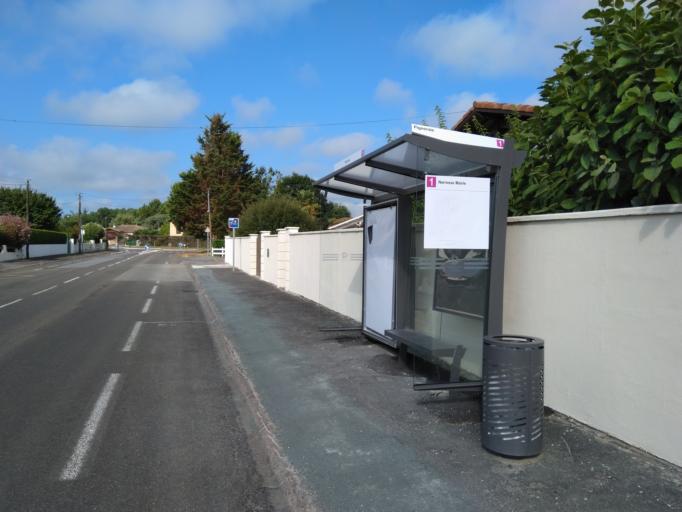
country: FR
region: Aquitaine
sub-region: Departement des Landes
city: Saint-Paul-les-Dax
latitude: 43.7326
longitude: -1.0843
